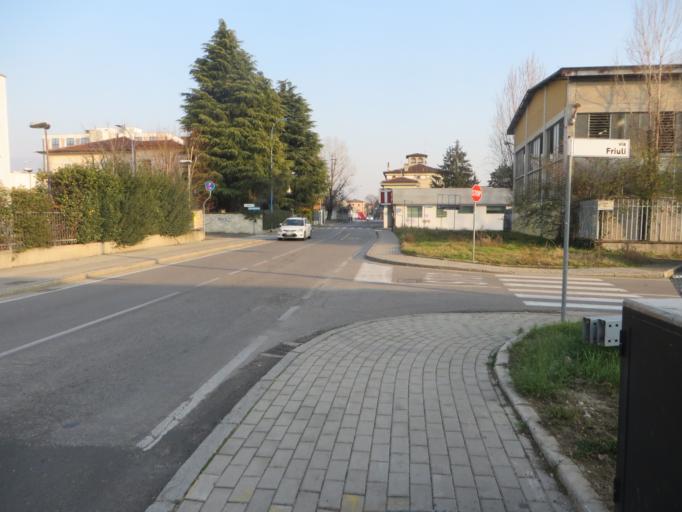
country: IT
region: Lombardy
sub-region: Provincia di Brescia
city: Brescia
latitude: 45.5255
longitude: 10.1952
